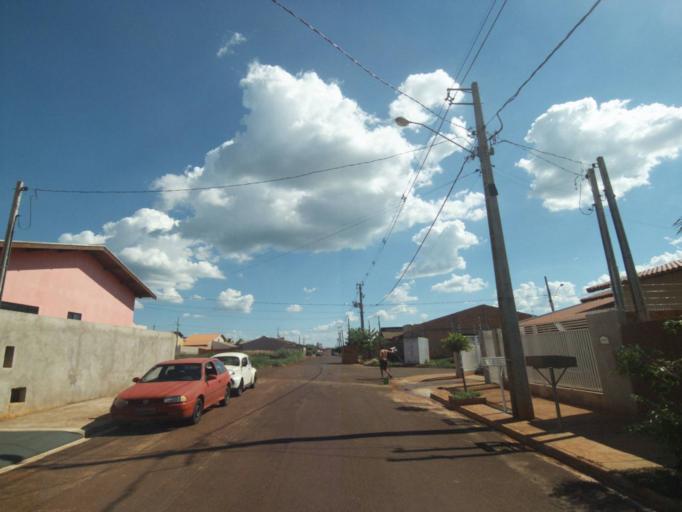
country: BR
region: Parana
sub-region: Sertanopolis
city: Sertanopolis
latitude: -23.0363
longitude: -50.8113
